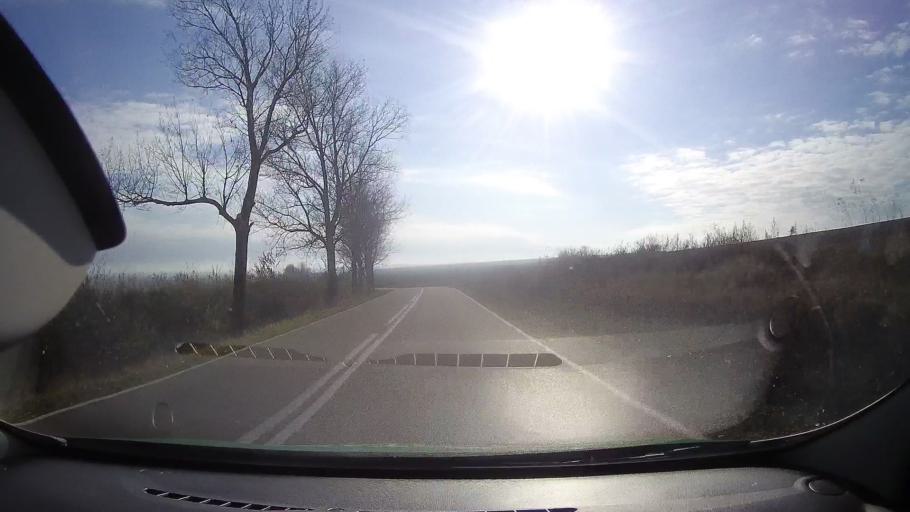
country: RO
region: Tulcea
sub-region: Comuna Mahmudia
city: Mahmudia
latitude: 45.0729
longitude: 29.0928
